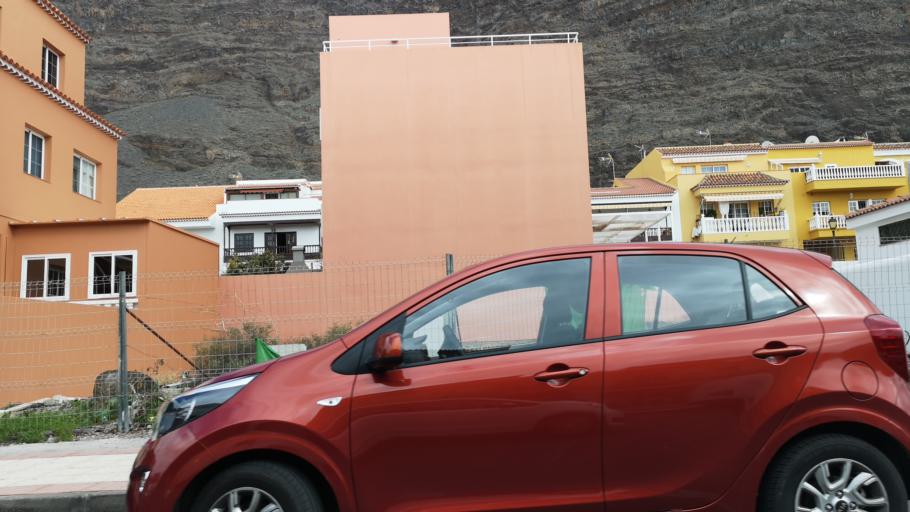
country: ES
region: Canary Islands
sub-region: Provincia de Santa Cruz de Tenerife
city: Alajero
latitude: 28.0859
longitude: -17.3345
